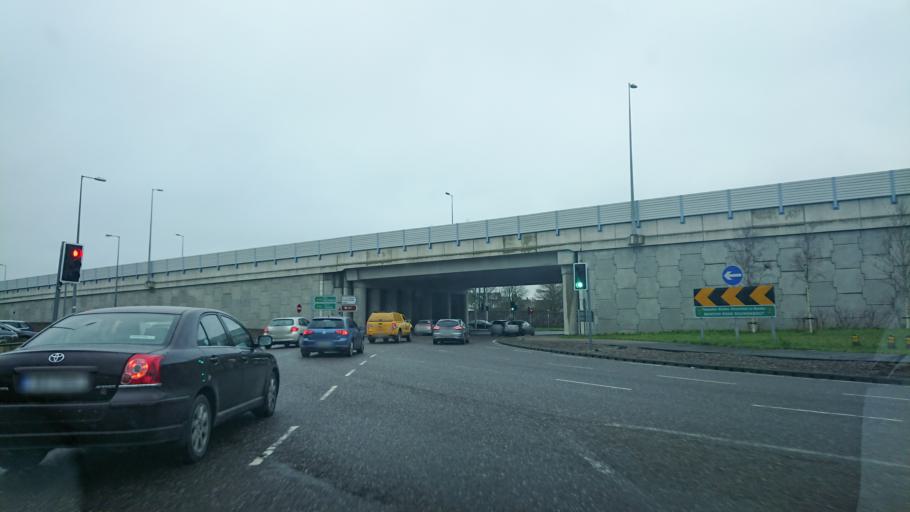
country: IE
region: Munster
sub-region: County Cork
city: Cork
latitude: 51.8739
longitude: -8.5236
